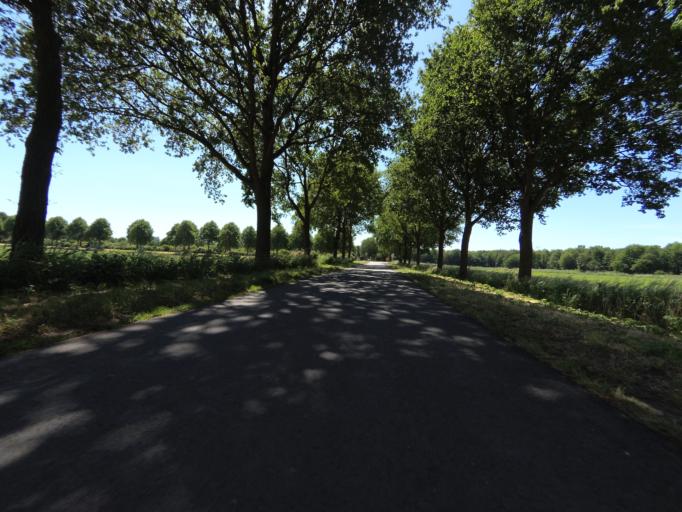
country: NL
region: Flevoland
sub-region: Gemeente Zeewolde
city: Zeewolde
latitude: 52.3259
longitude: 5.4993
